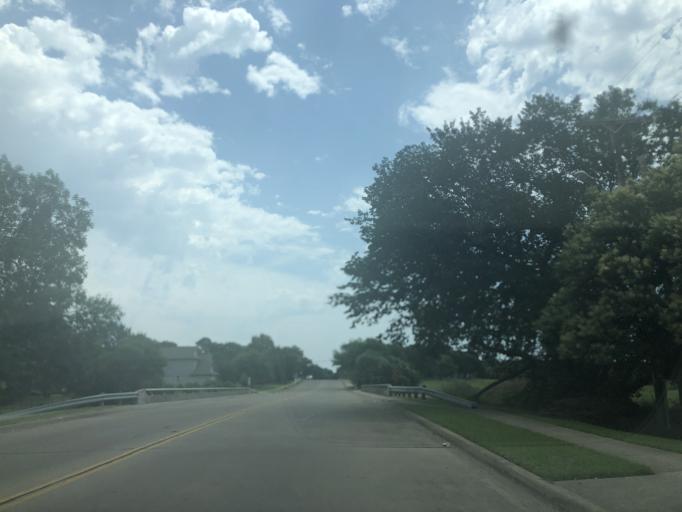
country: US
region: Texas
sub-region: Dallas County
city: Irving
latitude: 32.7939
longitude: -96.9369
